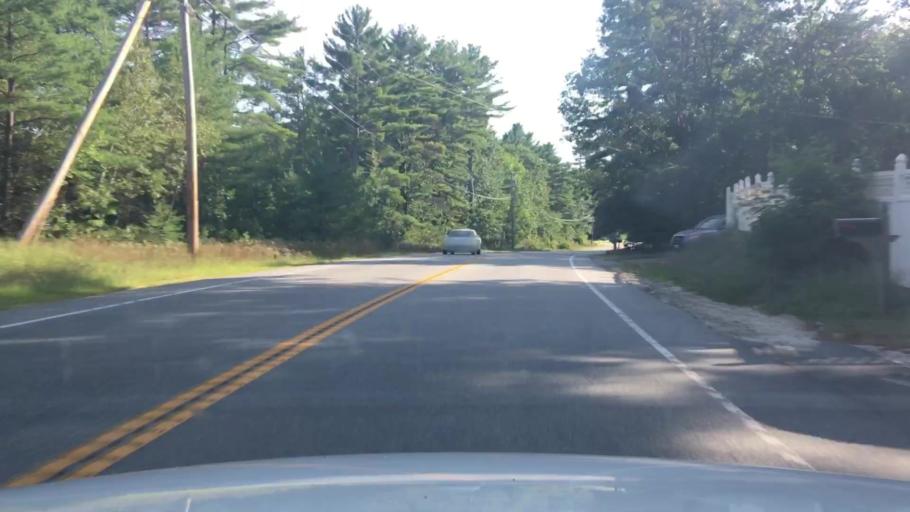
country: US
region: Maine
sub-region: Cumberland County
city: New Gloucester
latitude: 43.9257
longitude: -70.3107
